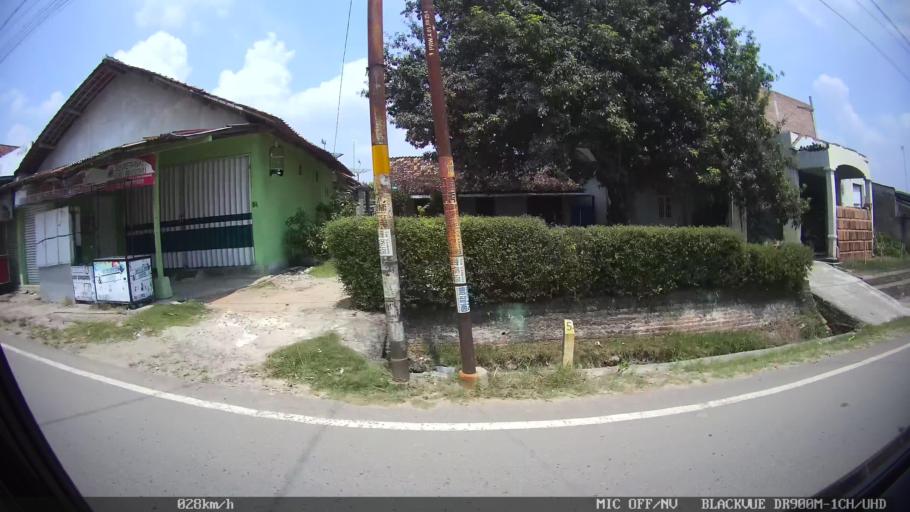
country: ID
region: Lampung
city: Pringsewu
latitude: -5.3608
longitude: 104.9771
